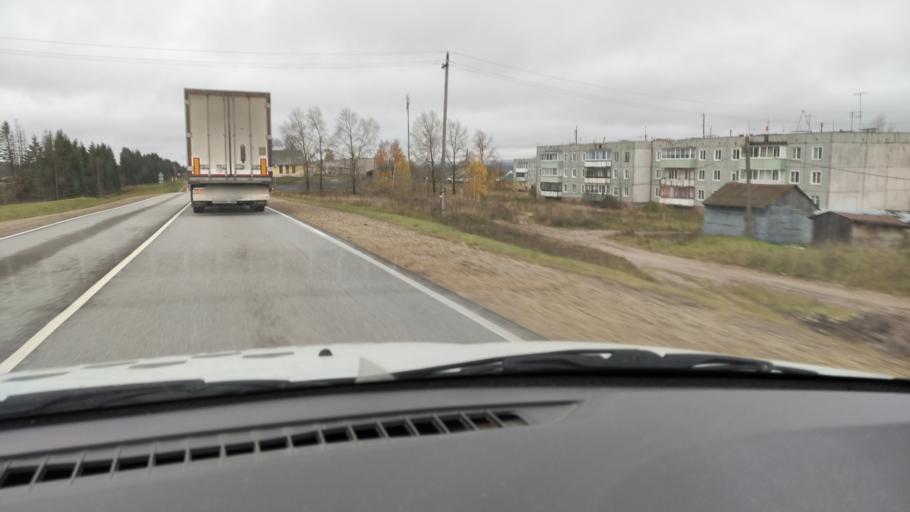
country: RU
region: Kirov
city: Slobodskoy
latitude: 58.7497
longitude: 50.3122
